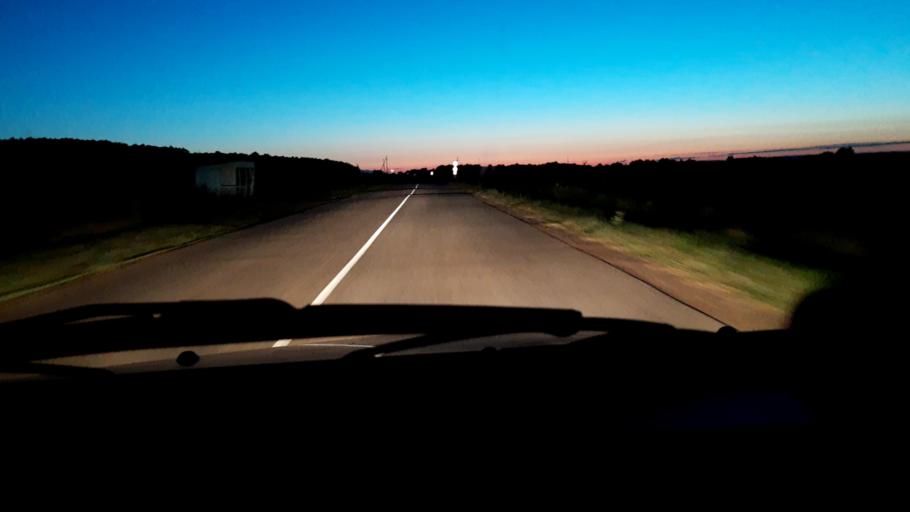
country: RU
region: Bashkortostan
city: Blagoveshchensk
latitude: 54.9333
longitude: 55.9006
